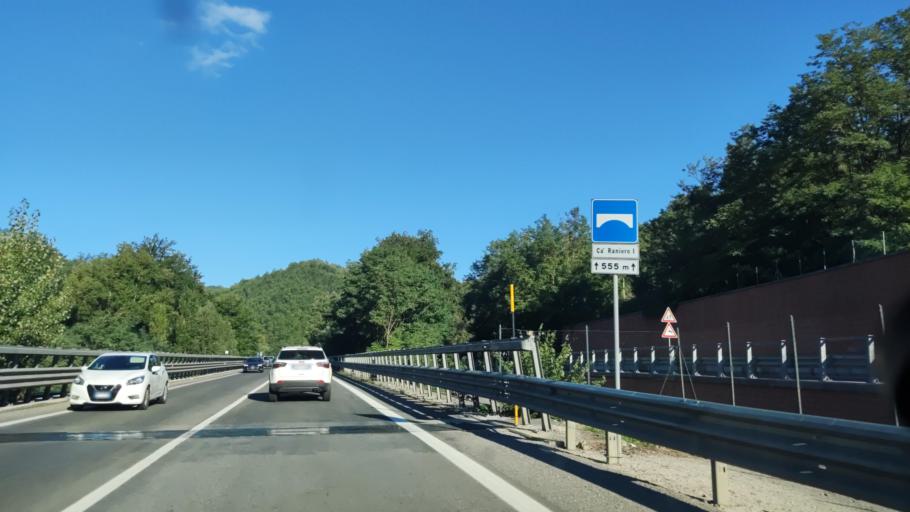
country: IT
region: The Marches
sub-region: Provincia di Pesaro e Urbino
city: Fermignano
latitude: 43.7045
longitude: 12.6597
